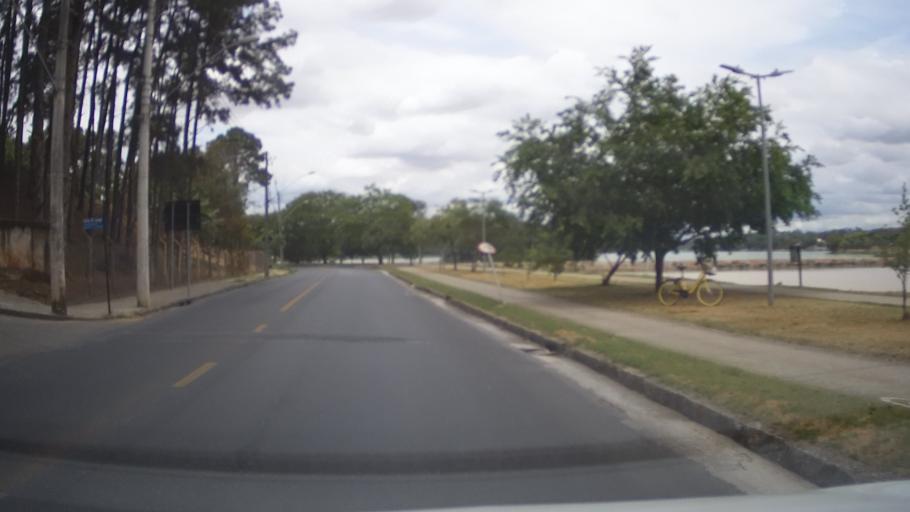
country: BR
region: Minas Gerais
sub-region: Belo Horizonte
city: Belo Horizonte
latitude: -19.8465
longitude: -43.9963
